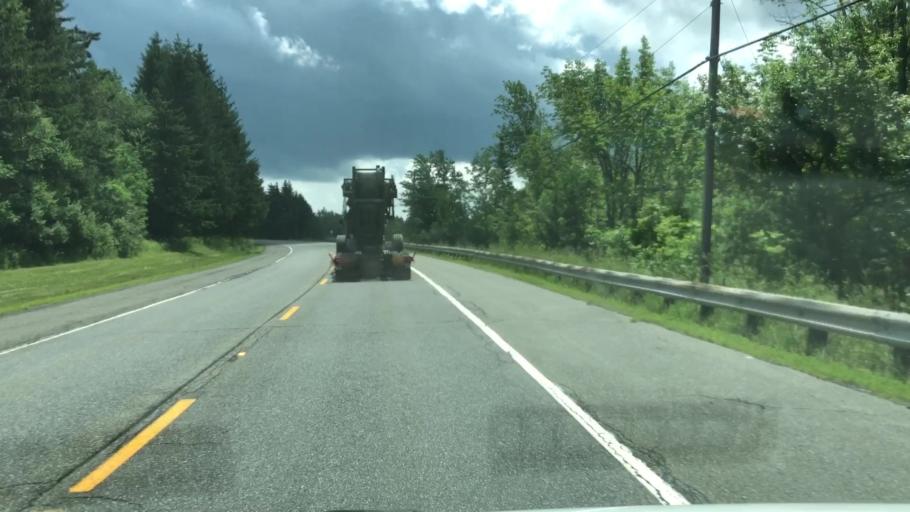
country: US
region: Massachusetts
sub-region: Berkshire County
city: Hinsdale
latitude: 42.5021
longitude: -73.0363
